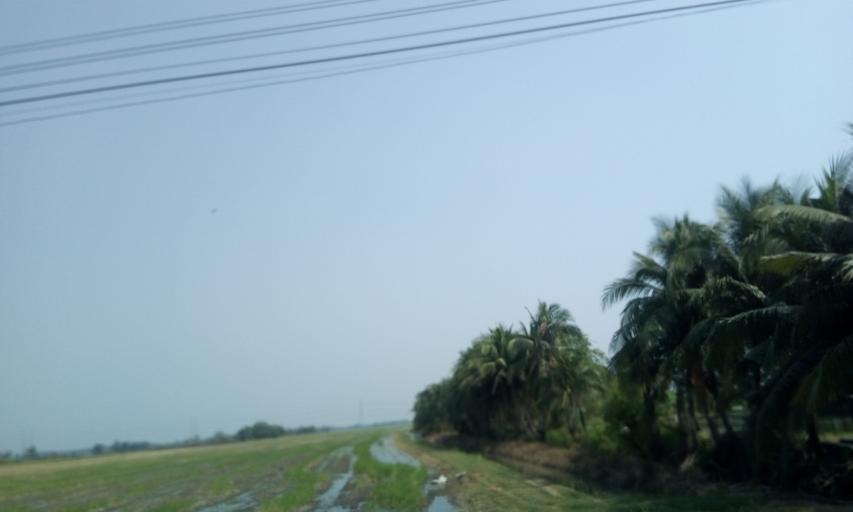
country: TH
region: Pathum Thani
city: Ban Rangsit
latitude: 14.0021
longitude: 100.7569
